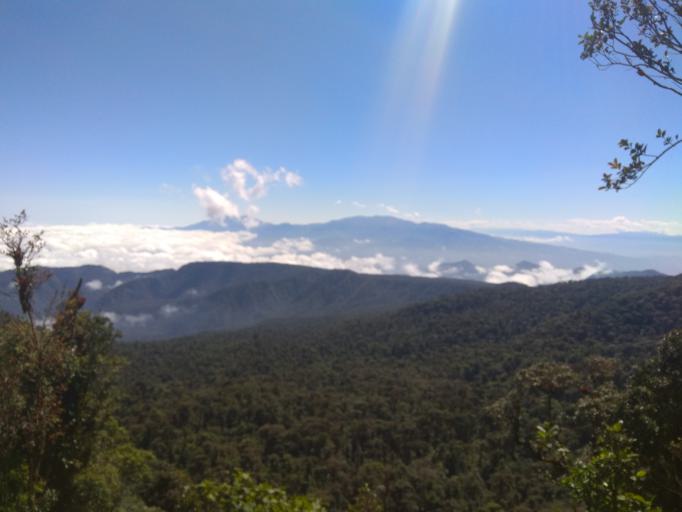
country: CR
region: Heredia
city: Santo Domingo
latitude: 10.1386
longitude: -84.0961
